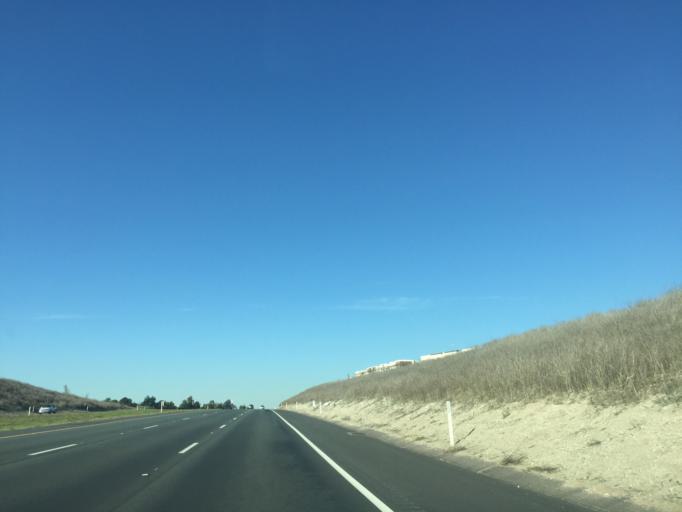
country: US
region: California
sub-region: San Diego County
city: Bonita
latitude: 32.6089
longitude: -116.9674
